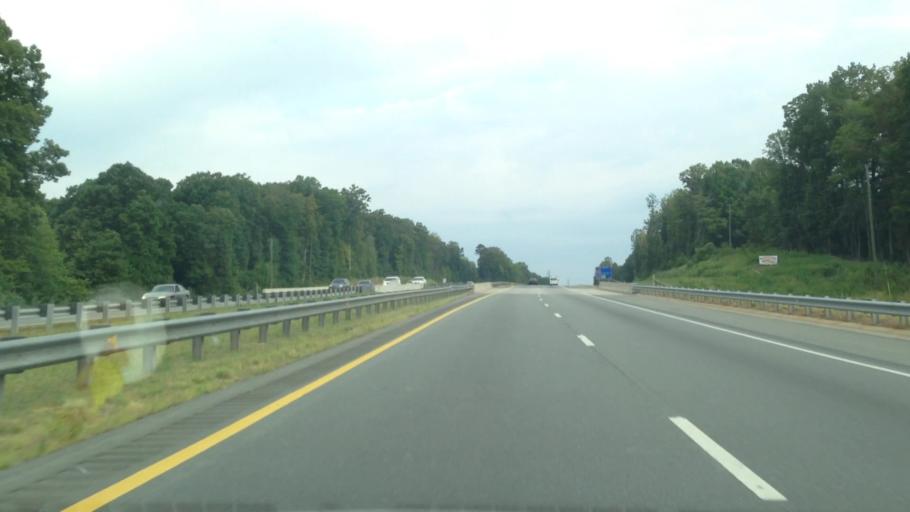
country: US
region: North Carolina
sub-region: Forsyth County
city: Tobaccoville
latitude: 36.2401
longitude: -80.3441
